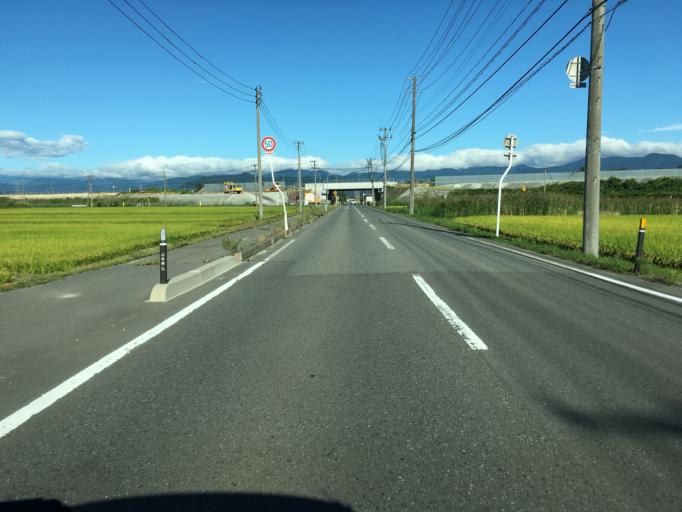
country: JP
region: Yamagata
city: Yonezawa
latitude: 37.9559
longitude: 140.1143
